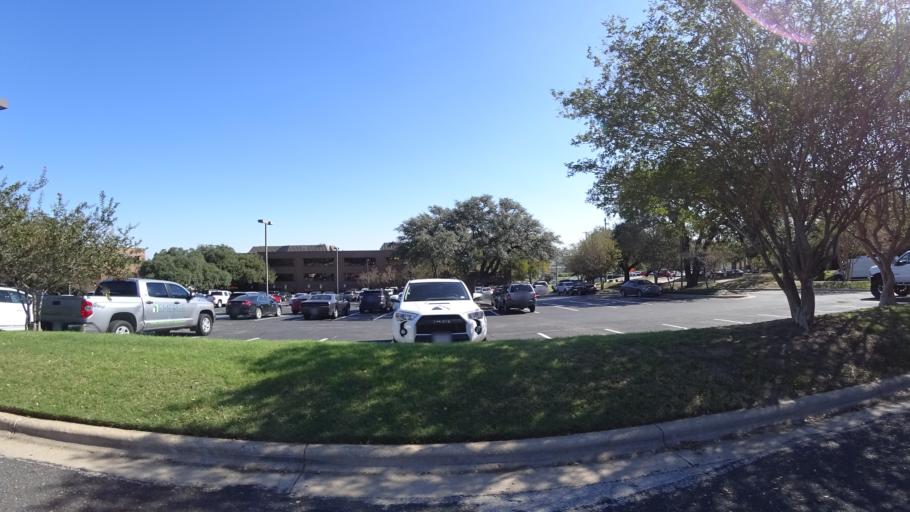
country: US
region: Texas
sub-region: Williamson County
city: Jollyville
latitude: 30.3695
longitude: -97.7445
